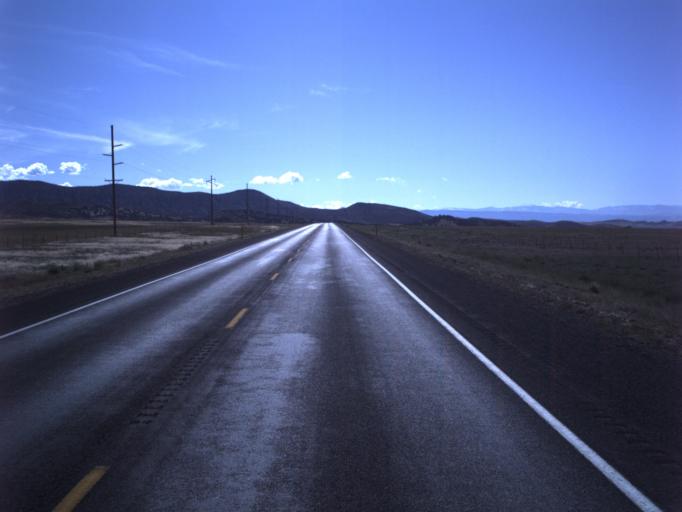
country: US
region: Utah
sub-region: Sanpete County
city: Gunnison
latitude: 39.2500
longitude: -111.8574
